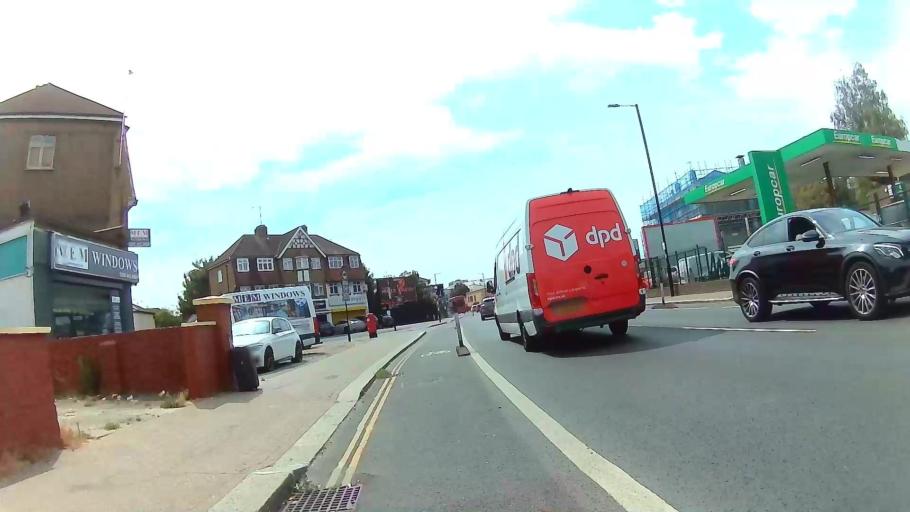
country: GB
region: England
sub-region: Hertfordshire
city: Waltham Cross
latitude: 51.6645
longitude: -0.0442
